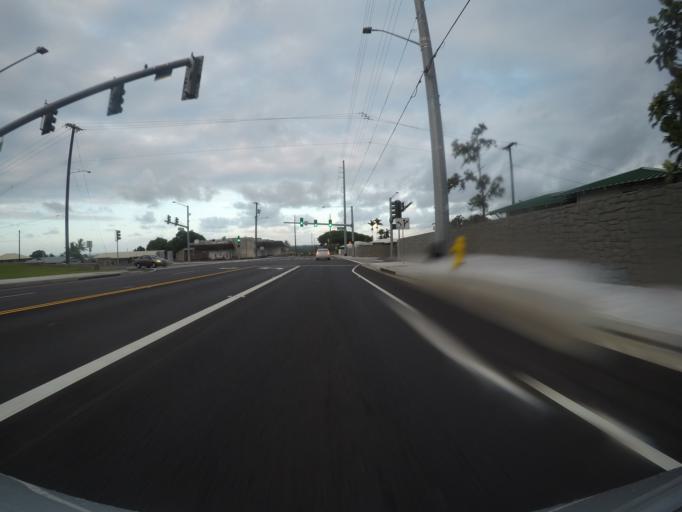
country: US
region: Hawaii
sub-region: Hawaii County
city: Hilo
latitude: 19.6838
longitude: -155.0809
